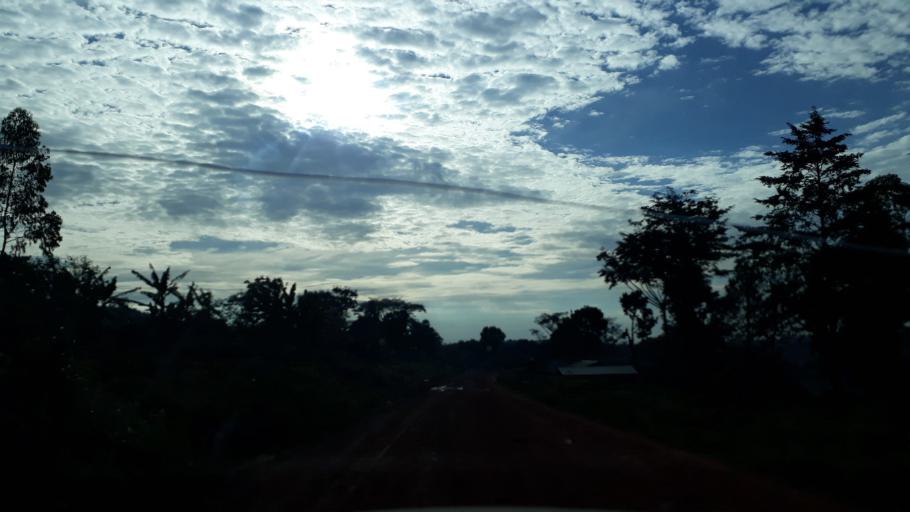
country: UG
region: Northern Region
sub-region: Zombo District
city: Paidha
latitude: 2.2526
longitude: 30.8691
